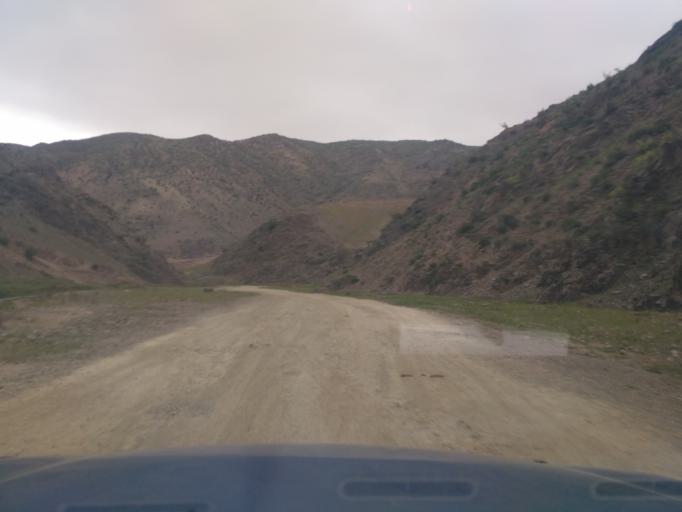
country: UZ
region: Jizzax
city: Zomin
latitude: 39.8551
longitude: 68.3893
